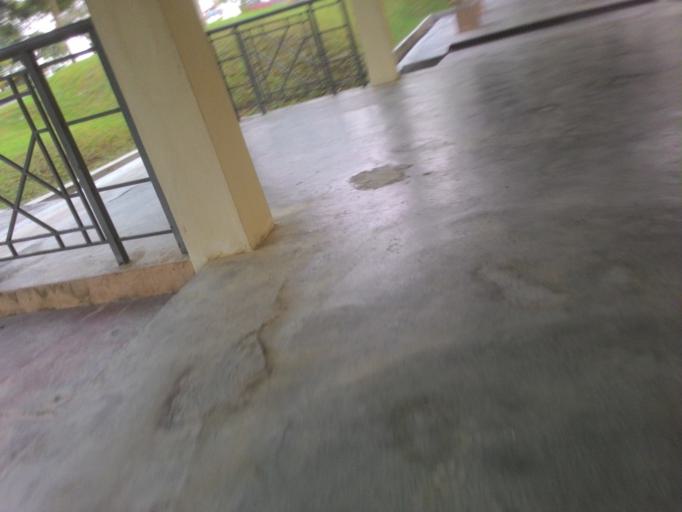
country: MY
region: Kedah
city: Kulim
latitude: 5.3829
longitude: 100.5764
